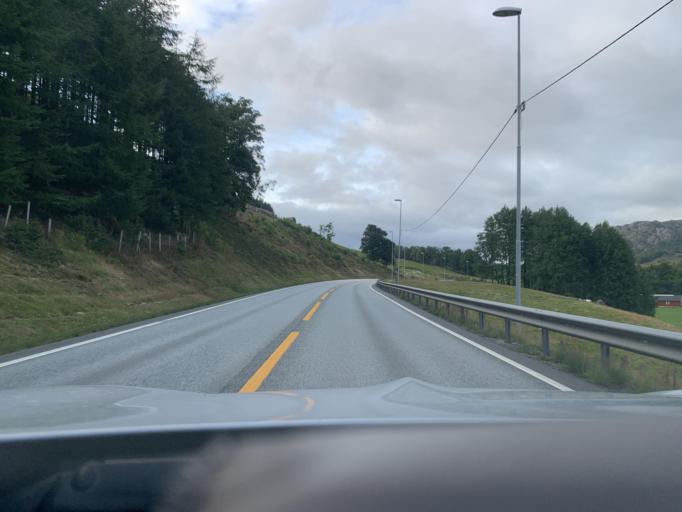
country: NO
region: Rogaland
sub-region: Bjerkreim
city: Vikesa
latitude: 58.6048
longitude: 6.0840
